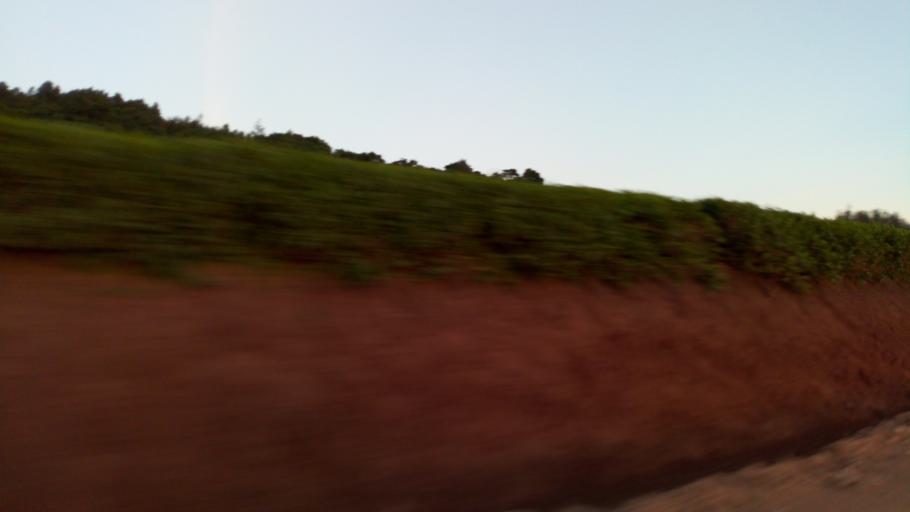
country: KE
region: Nyamira District
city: Nyamira
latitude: -0.5922
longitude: 35.0559
